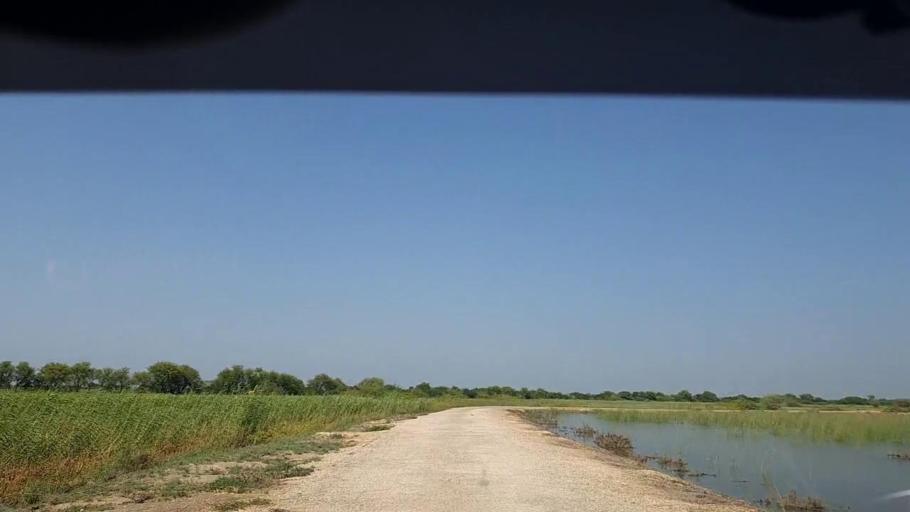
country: PK
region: Sindh
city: Badin
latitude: 24.4602
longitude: 68.7678
